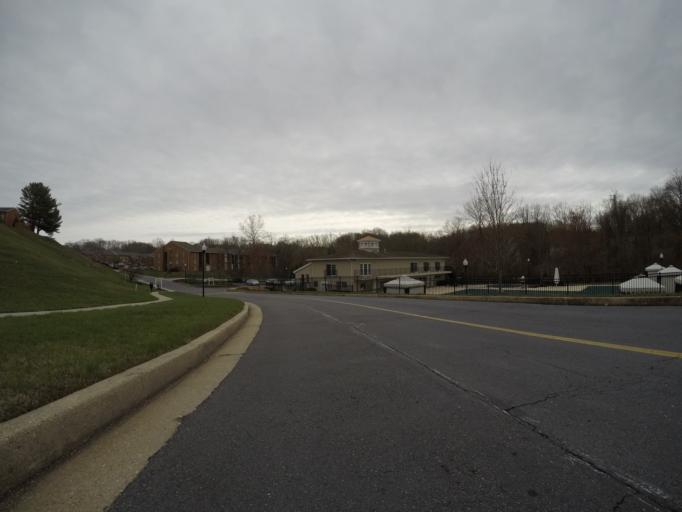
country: US
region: Maryland
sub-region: Howard County
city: Ellicott City
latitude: 39.2828
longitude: -76.8044
